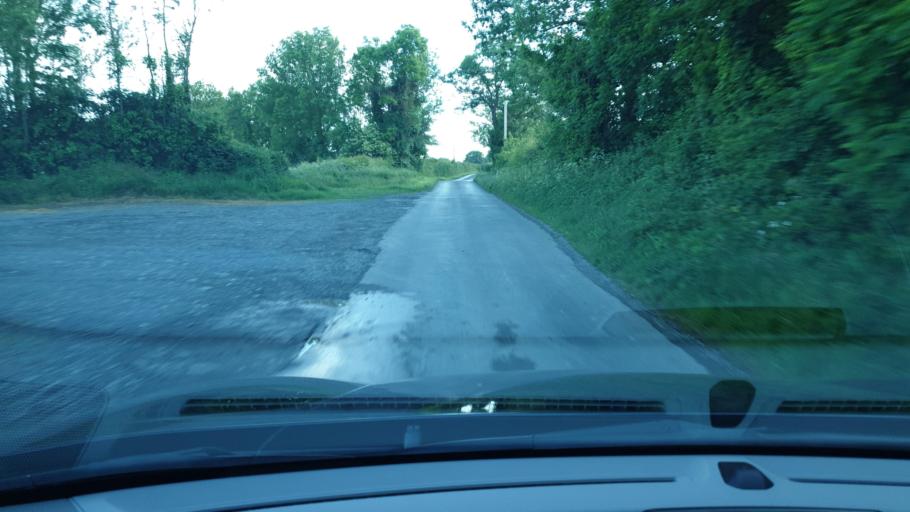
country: IE
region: Leinster
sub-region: An Mhi
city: Ashbourne
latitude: 53.4834
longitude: -6.3488
